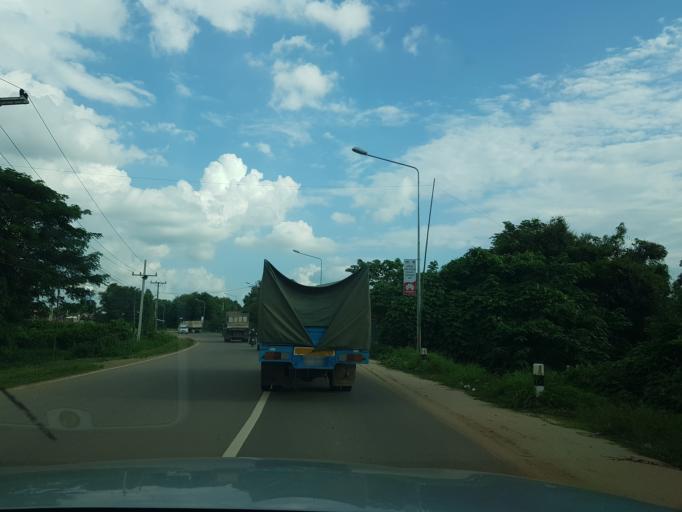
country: TH
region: Nong Khai
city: Si Chiang Mai
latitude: 17.9762
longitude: 102.4969
